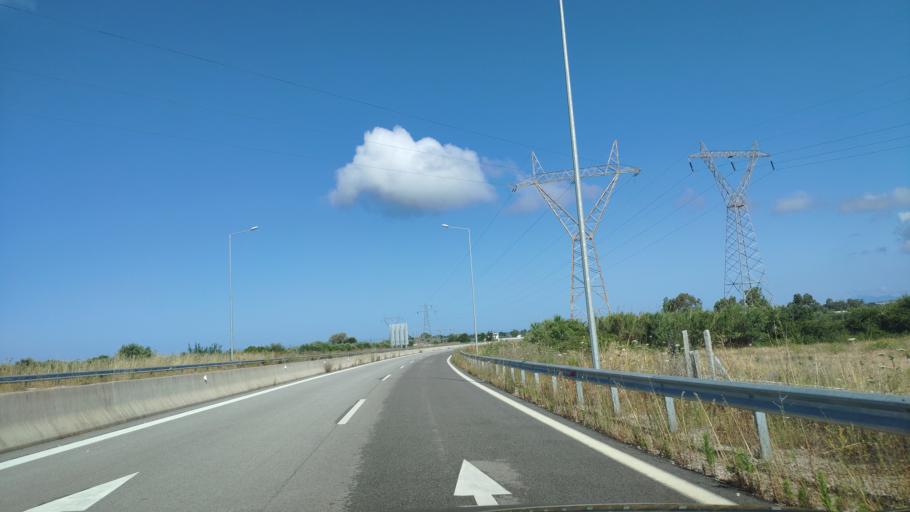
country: GR
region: Epirus
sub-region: Nomos Prevezis
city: Preveza
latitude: 38.9130
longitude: 20.7983
